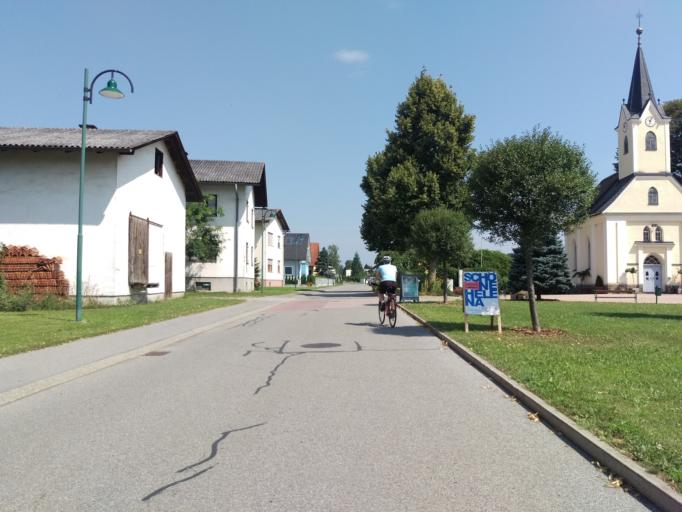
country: AT
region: Styria
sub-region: Politischer Bezirk Graz-Umgebung
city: Werndorf
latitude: 46.9239
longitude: 15.4903
